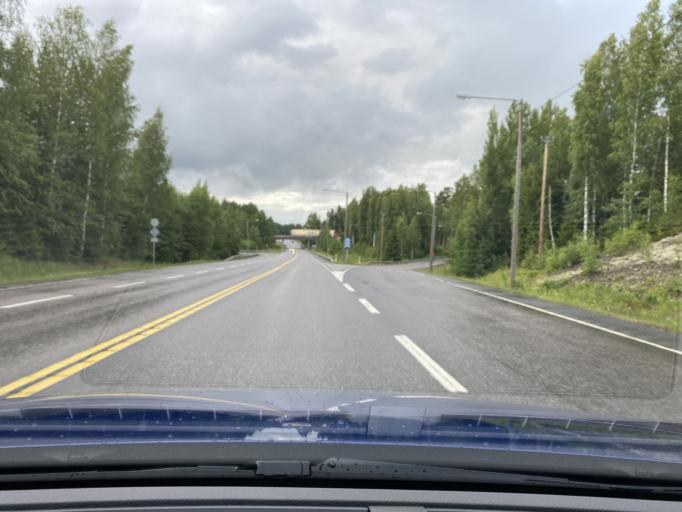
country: FI
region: Uusimaa
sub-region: Helsinki
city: Hyvinge
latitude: 60.5609
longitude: 24.8177
